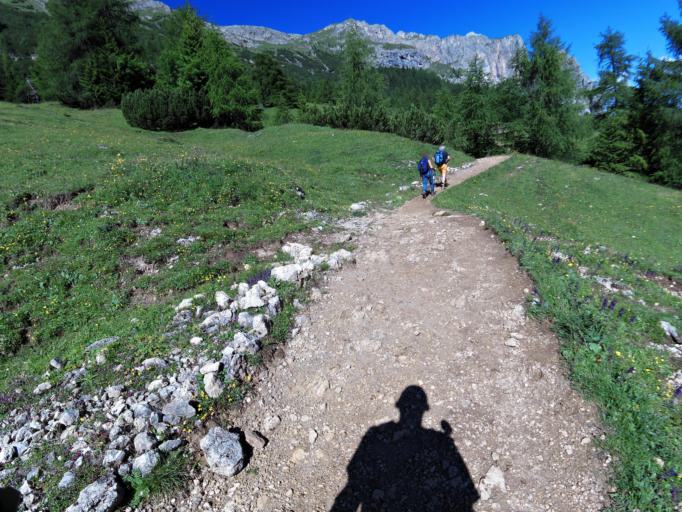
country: IT
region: Trentino-Alto Adige
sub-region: Bolzano
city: Siusi
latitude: 46.5130
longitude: 11.5989
